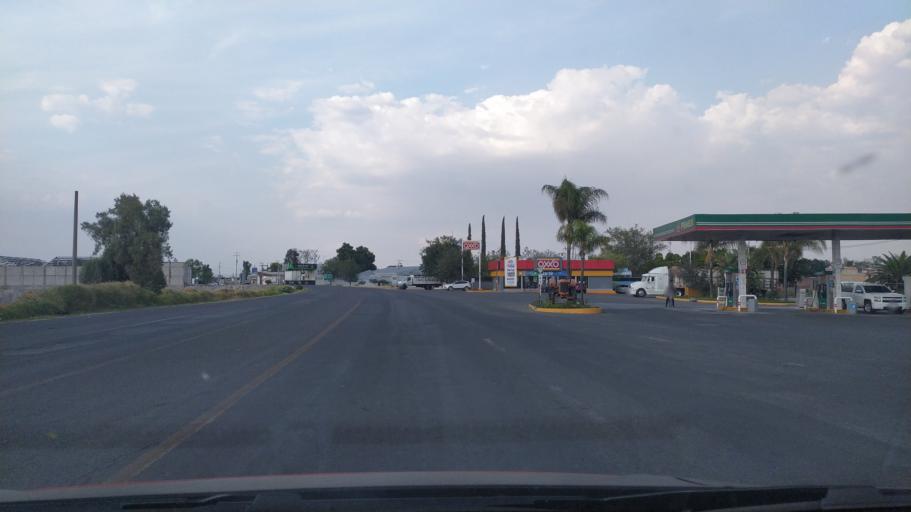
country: MX
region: Michoacan
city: Brisenas
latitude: 20.2773
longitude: -102.5576
